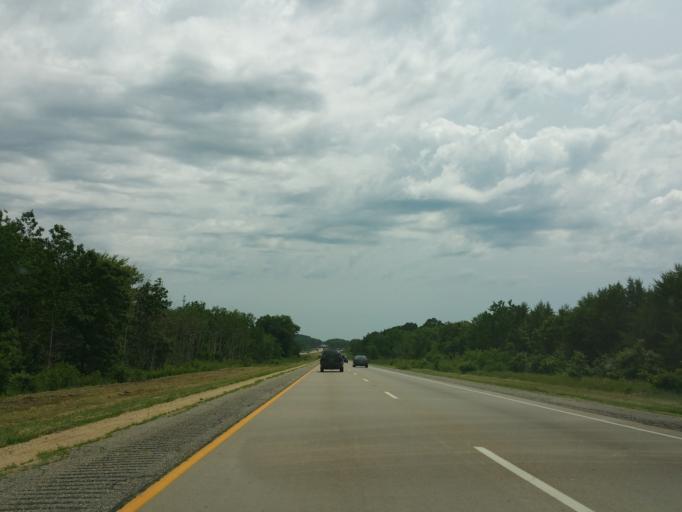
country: US
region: Wisconsin
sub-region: Columbia County
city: Wisconsin Dells
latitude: 43.6870
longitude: -89.8448
